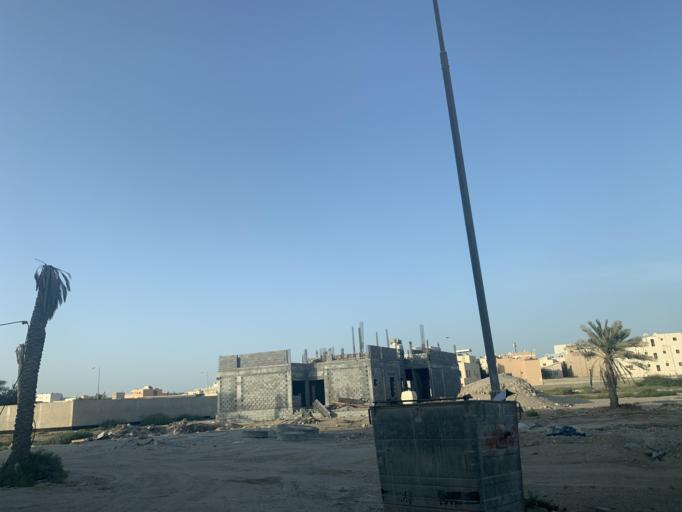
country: BH
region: Manama
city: Jidd Hafs
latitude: 26.2064
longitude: 50.4538
